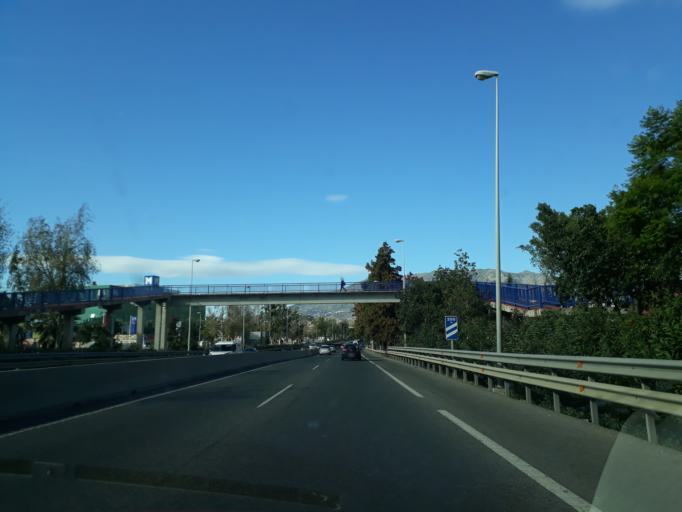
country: ES
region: Andalusia
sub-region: Provincia de Malaga
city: Fuengirola
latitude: 36.5357
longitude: -4.6334
